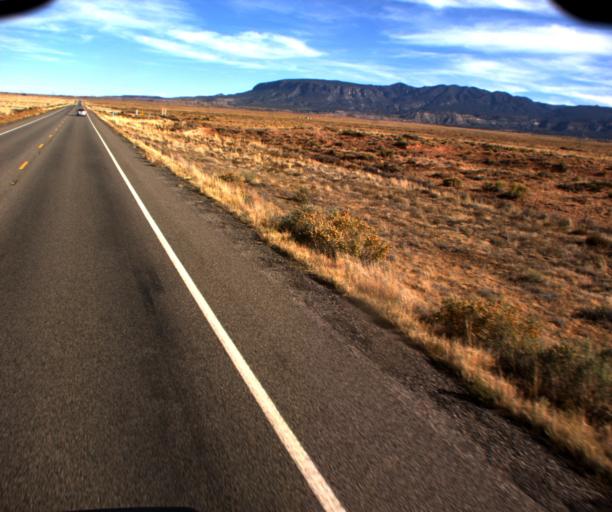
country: US
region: Arizona
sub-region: Apache County
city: Lukachukai
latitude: 36.9450
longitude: -109.2654
